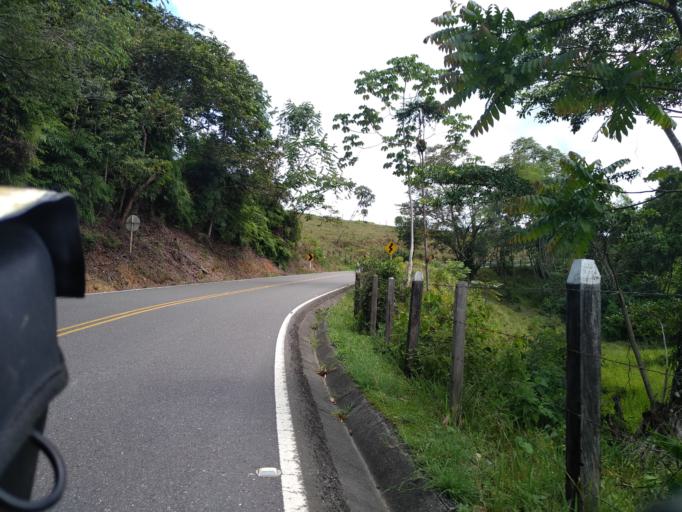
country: CO
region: Santander
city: Cimitarra
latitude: 6.4434
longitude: -74.0174
